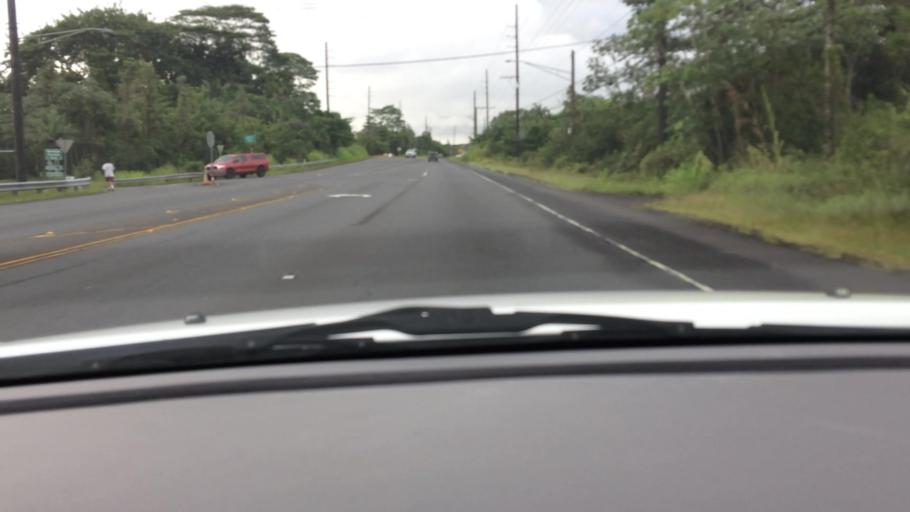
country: US
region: Hawaii
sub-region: Hawaii County
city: Ainaloa
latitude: 19.5470
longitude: -154.9789
